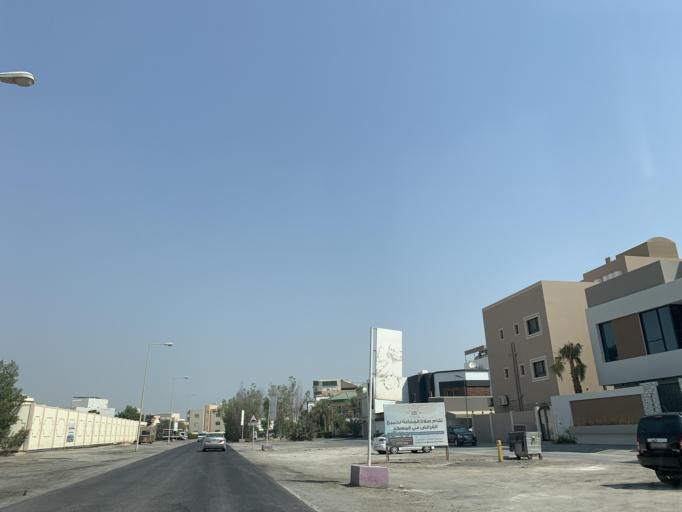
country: BH
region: Northern
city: Madinat `Isa
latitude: 26.1947
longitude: 50.5150
